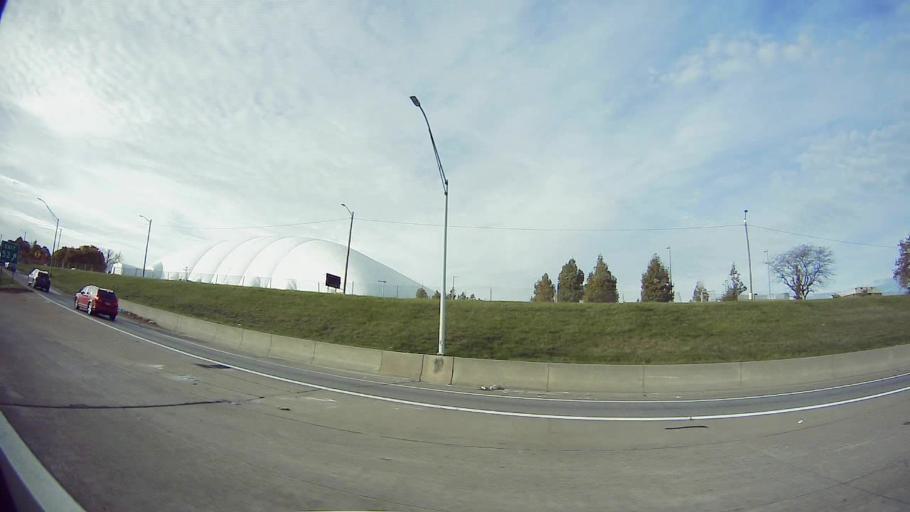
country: US
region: Michigan
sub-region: Wayne County
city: Detroit
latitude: 42.3531
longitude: -83.0495
